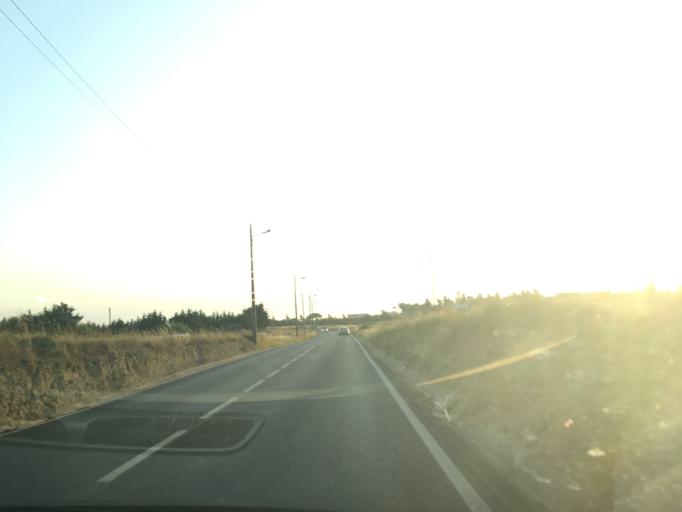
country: PT
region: Lisbon
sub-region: Sintra
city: Colares
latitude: 38.8274
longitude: -9.4155
